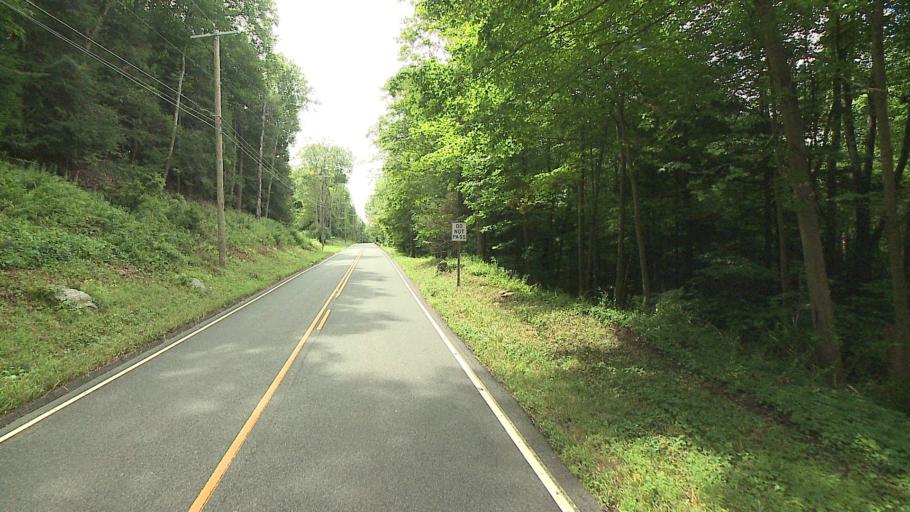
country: US
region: Connecticut
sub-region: Litchfield County
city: New Milford
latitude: 41.5908
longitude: -73.3217
